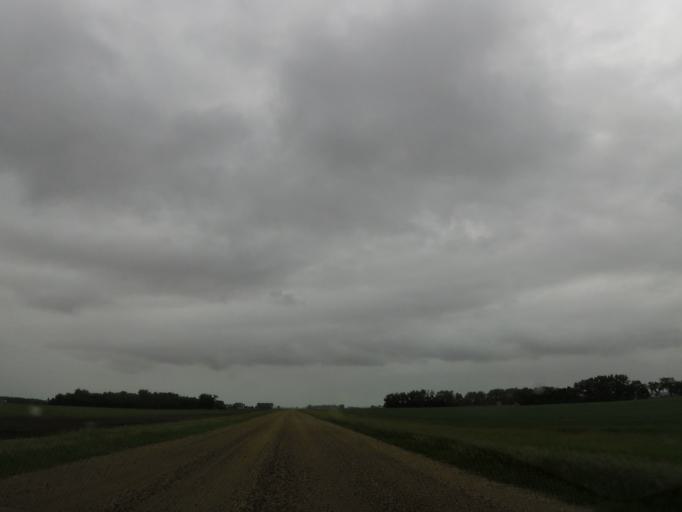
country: US
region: North Dakota
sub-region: Walsh County
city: Grafton
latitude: 48.5376
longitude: -97.3000
